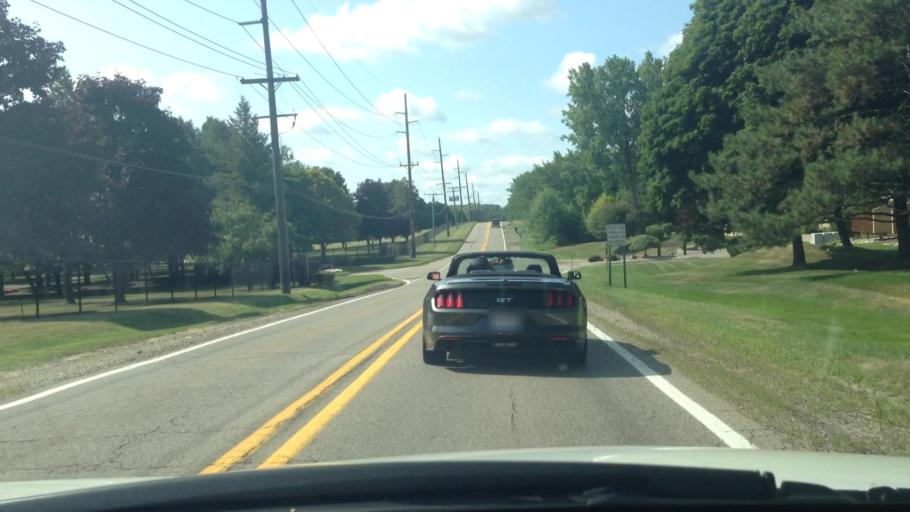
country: US
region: Michigan
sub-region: Oakland County
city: Waterford
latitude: 42.7021
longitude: -83.4417
